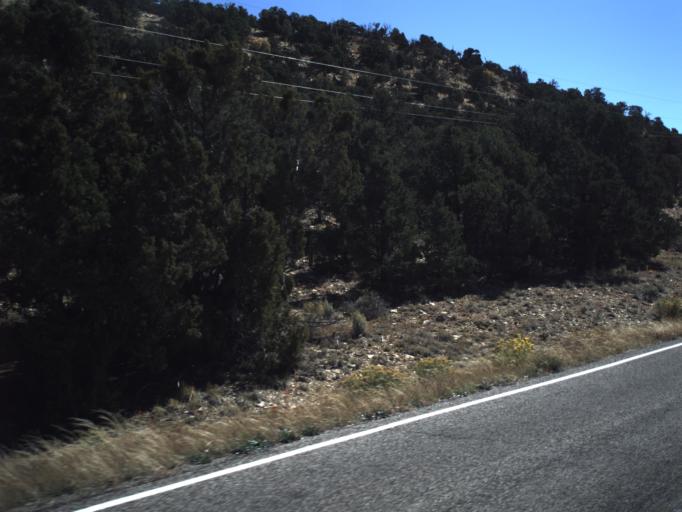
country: US
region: Utah
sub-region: Wayne County
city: Loa
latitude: 37.9370
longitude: -111.4314
